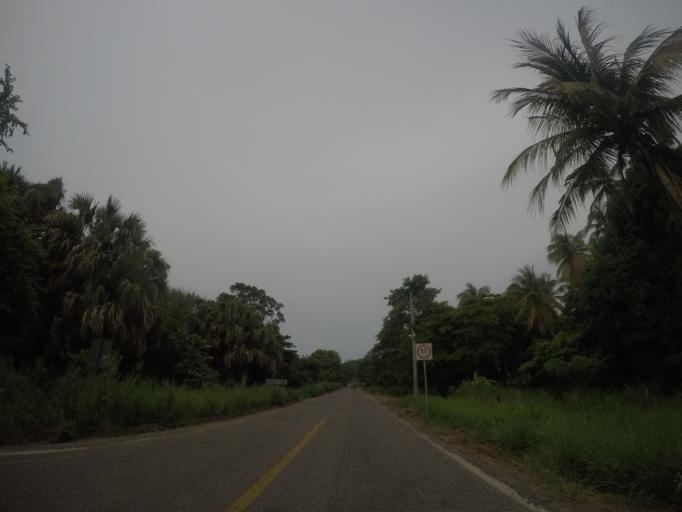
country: MX
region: Oaxaca
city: San Pedro Mixtepec
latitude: 15.9557
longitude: -97.2196
